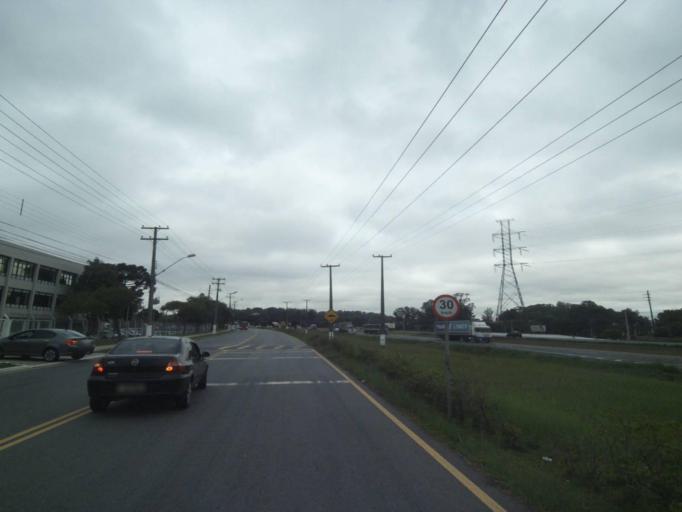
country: BR
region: Parana
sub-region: Araucaria
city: Araucaria
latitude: -25.5281
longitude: -49.3276
